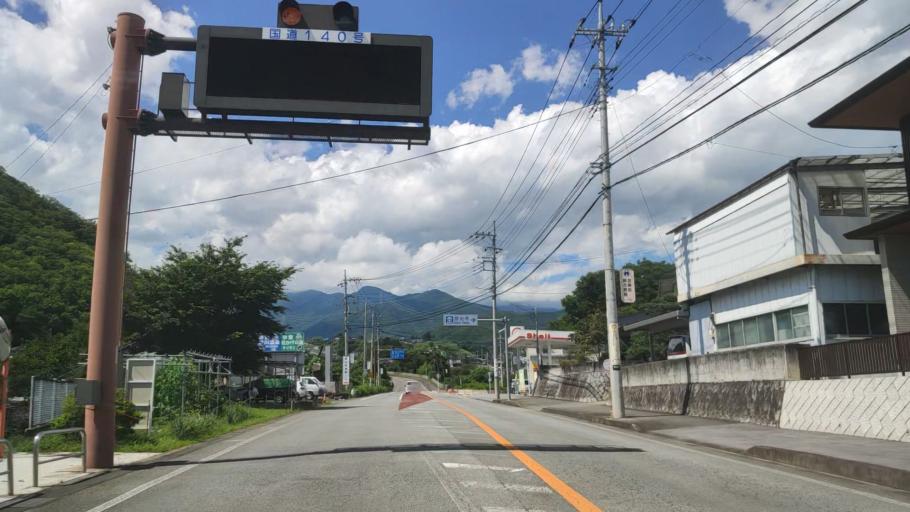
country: JP
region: Yamanashi
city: Enzan
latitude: 35.7335
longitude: 138.7119
